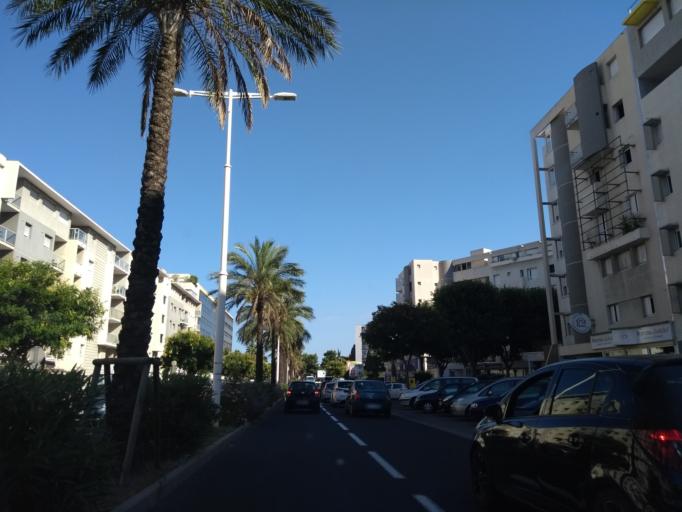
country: FR
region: Languedoc-Roussillon
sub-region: Departement des Pyrenees-Orientales
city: Perpignan
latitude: 42.6881
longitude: 2.9049
